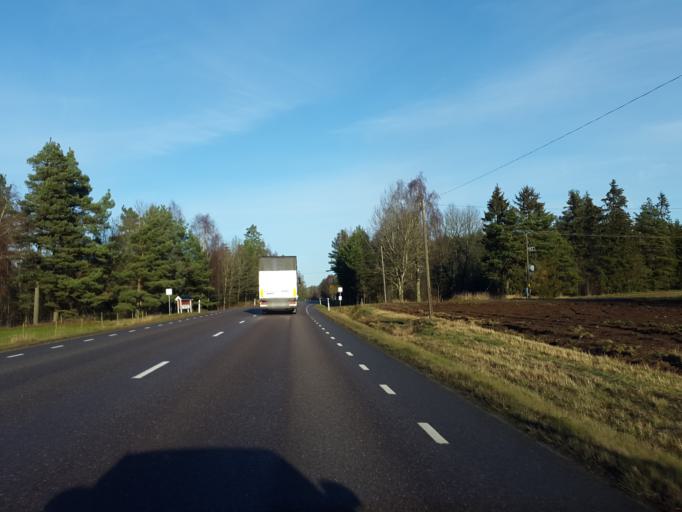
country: SE
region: Vaestra Goetaland
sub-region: Vargarda Kommun
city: Vargarda
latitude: 58.0023
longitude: 12.8125
